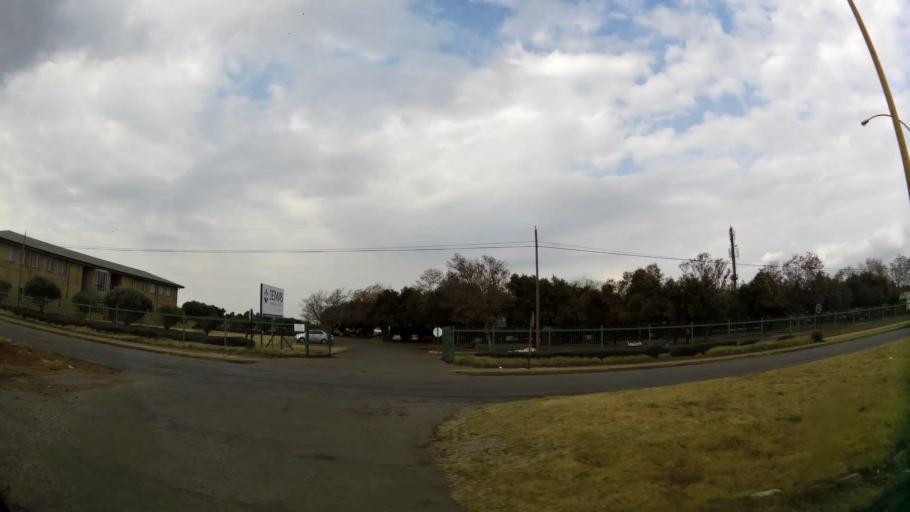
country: ZA
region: Gauteng
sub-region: Sedibeng District Municipality
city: Vanderbijlpark
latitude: -26.6765
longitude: 27.8182
